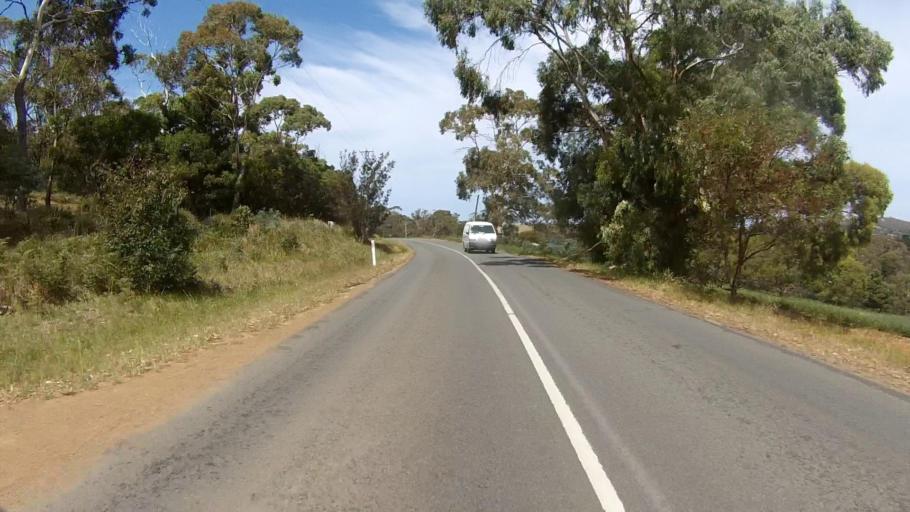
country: AU
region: Tasmania
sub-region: Kingborough
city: Taroona
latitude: -43.0165
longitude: 147.4167
